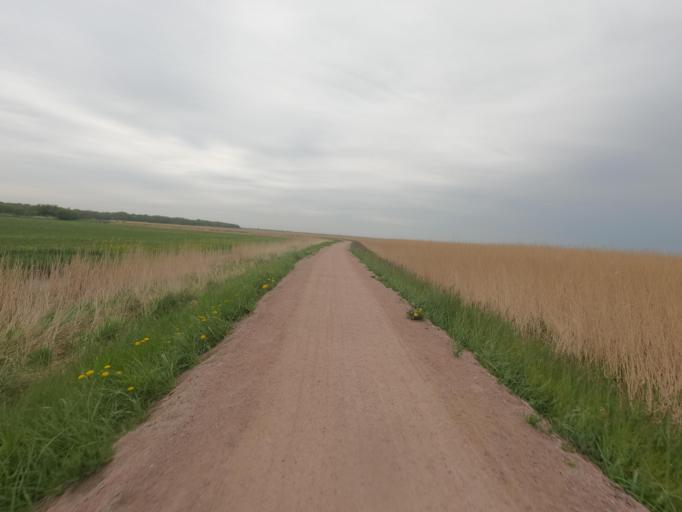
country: DE
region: Mecklenburg-Vorpommern
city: Saal
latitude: 54.3758
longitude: 12.4314
